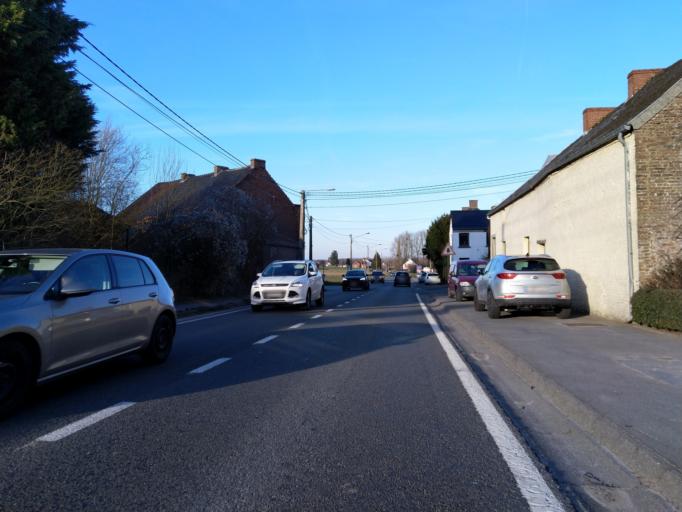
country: BE
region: Wallonia
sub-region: Province du Hainaut
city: Frameries
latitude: 50.3952
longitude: 3.9140
